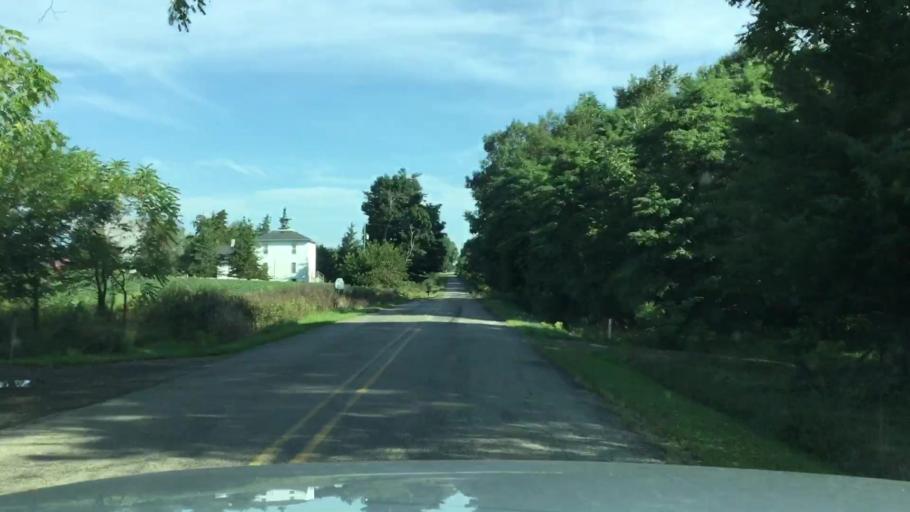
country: US
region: Michigan
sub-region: Lenawee County
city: Hudson
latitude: 41.8911
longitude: -84.4203
